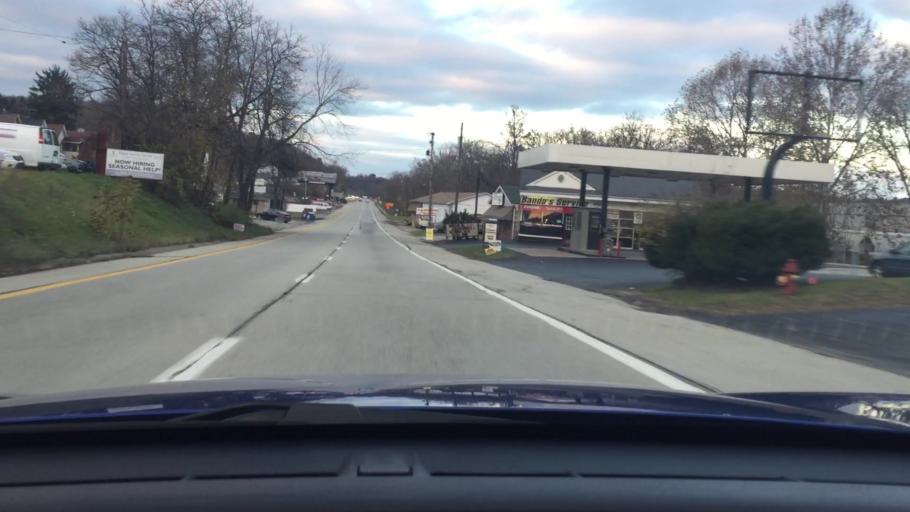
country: US
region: Pennsylvania
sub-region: Westmoreland County
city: Youngwood
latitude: 40.2434
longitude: -79.5755
